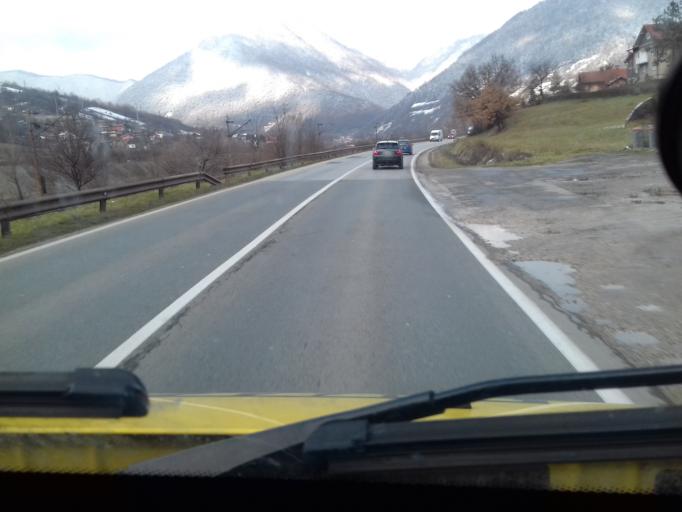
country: BA
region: Federation of Bosnia and Herzegovina
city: Zenica
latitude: 44.2386
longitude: 17.8981
